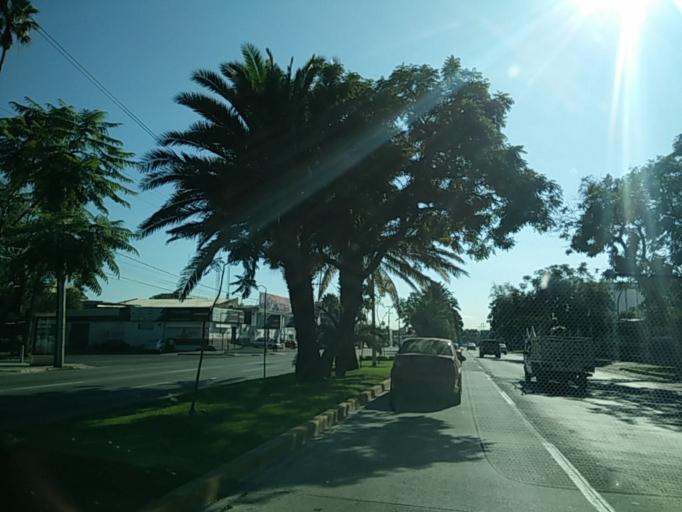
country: MX
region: Jalisco
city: Guadalajara
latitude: 20.6608
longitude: -103.3602
